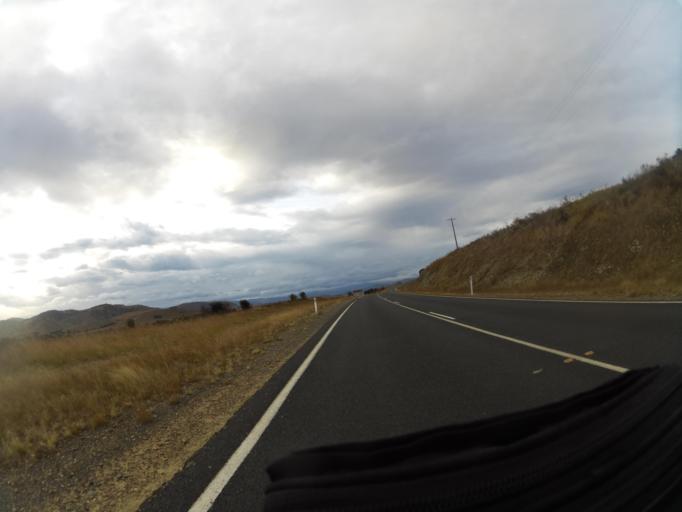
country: AU
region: New South Wales
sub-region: Snowy River
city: Jindabyne
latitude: -36.0811
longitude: 147.9757
